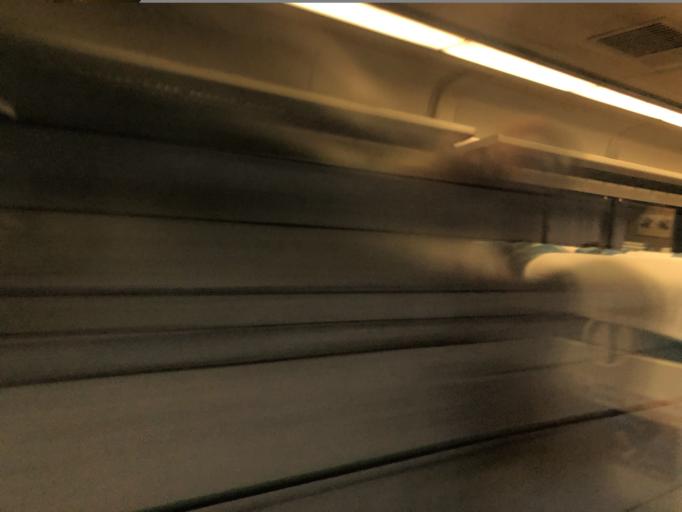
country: JP
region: Kochi
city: Nakamura
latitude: 33.0385
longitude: 133.0786
